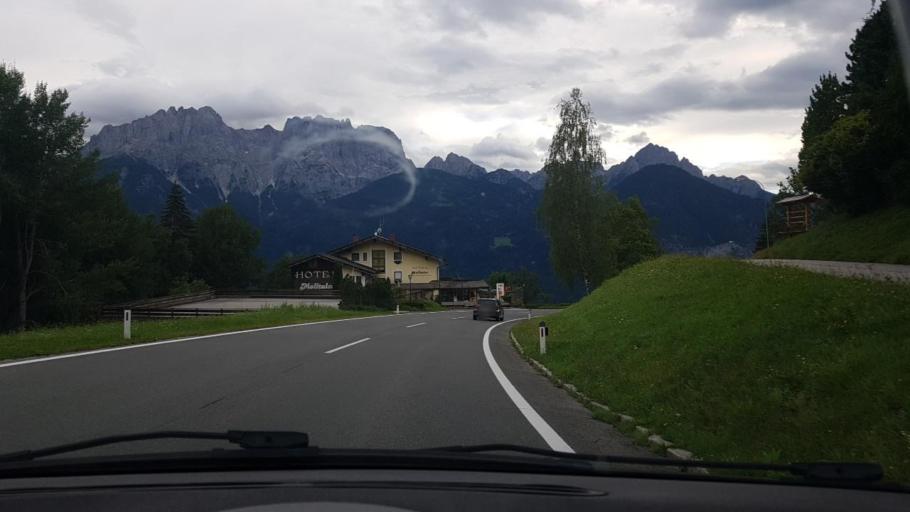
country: AT
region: Tyrol
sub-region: Politischer Bezirk Lienz
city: Dolsach
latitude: 46.8405
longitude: 12.8494
